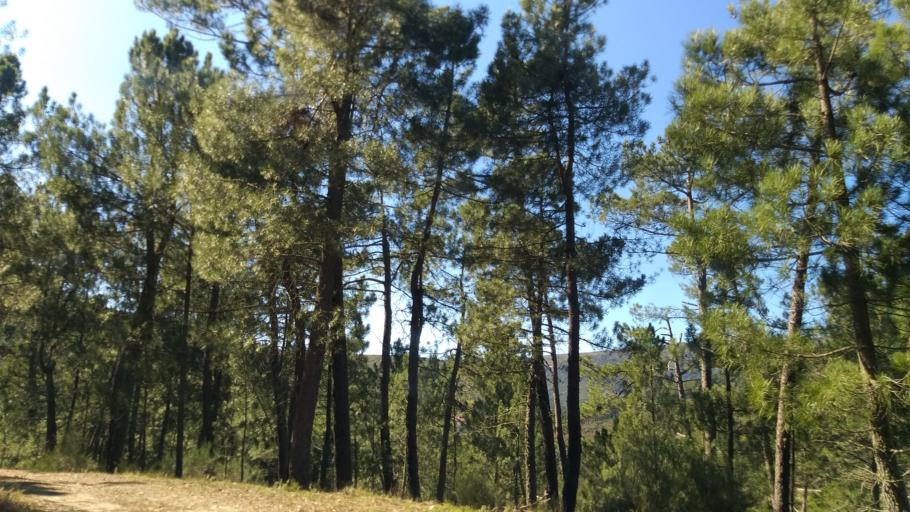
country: PT
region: Guarda
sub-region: Manteigas
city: Manteigas
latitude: 40.4430
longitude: -7.5098
